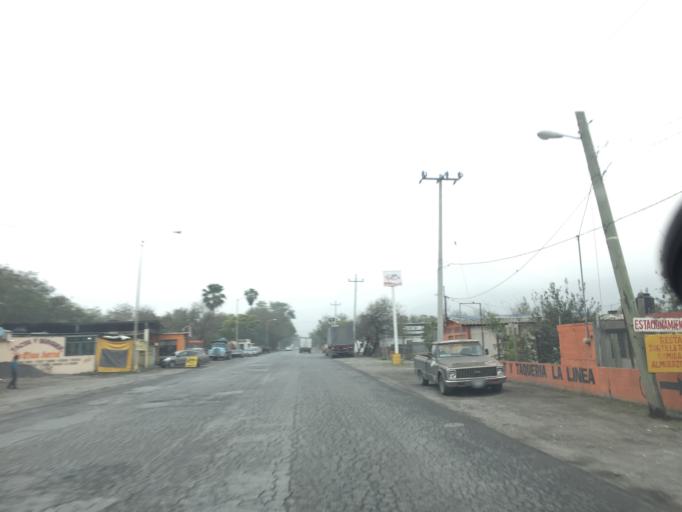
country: MX
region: Nuevo Leon
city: Mina
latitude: 25.9683
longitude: -100.4386
